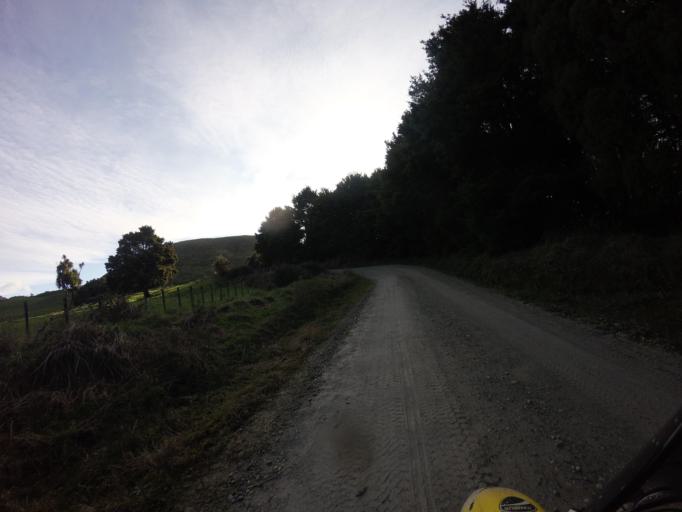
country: NZ
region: Hawke's Bay
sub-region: Wairoa District
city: Wairoa
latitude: -38.7459
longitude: 177.5233
